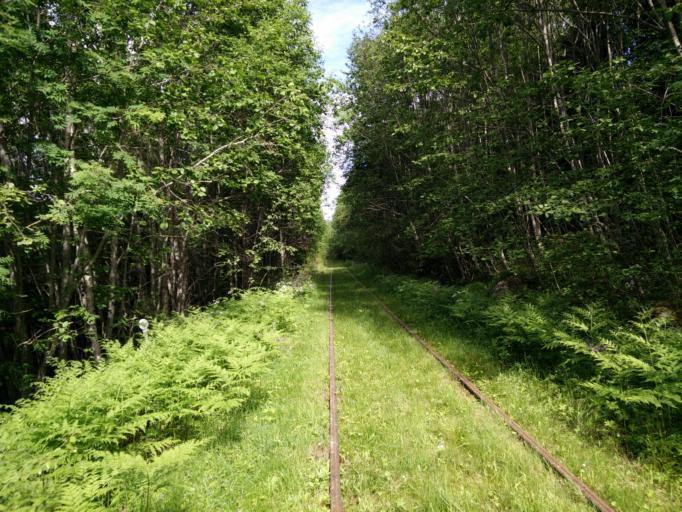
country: SE
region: Gaevleborg
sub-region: Hudiksvalls Kommun
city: Delsbo
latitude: 61.8006
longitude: 16.4018
